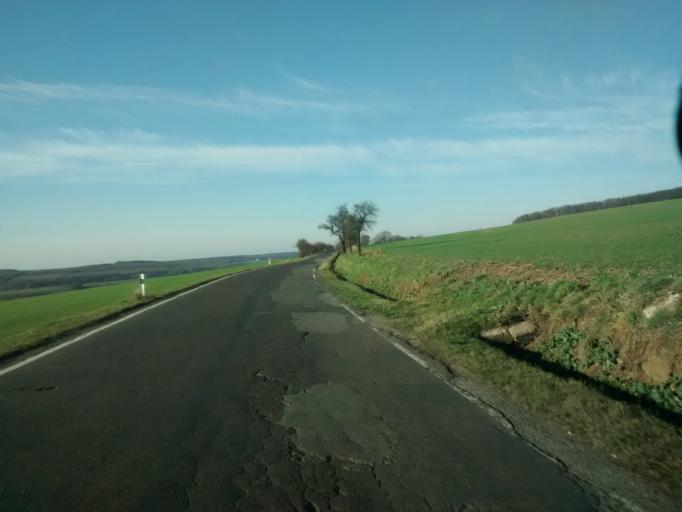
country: CZ
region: Kralovehradecky
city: Liban
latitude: 50.3719
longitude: 15.1521
